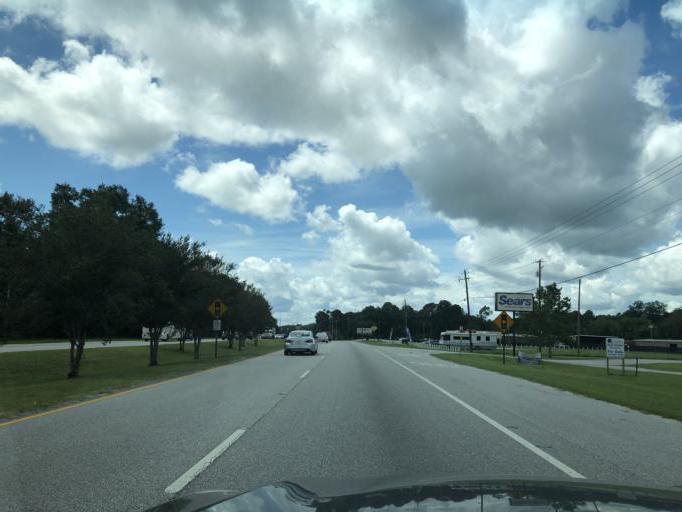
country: US
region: Alabama
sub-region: Barbour County
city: Eufaula
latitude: 31.9197
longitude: -85.1471
